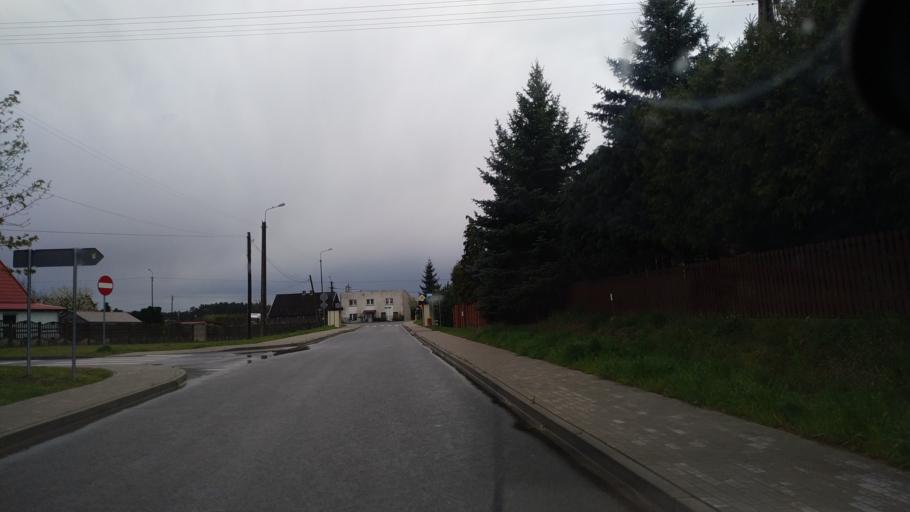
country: PL
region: Pomeranian Voivodeship
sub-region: Powiat starogardzki
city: Osiek
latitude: 53.6375
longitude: 18.4806
